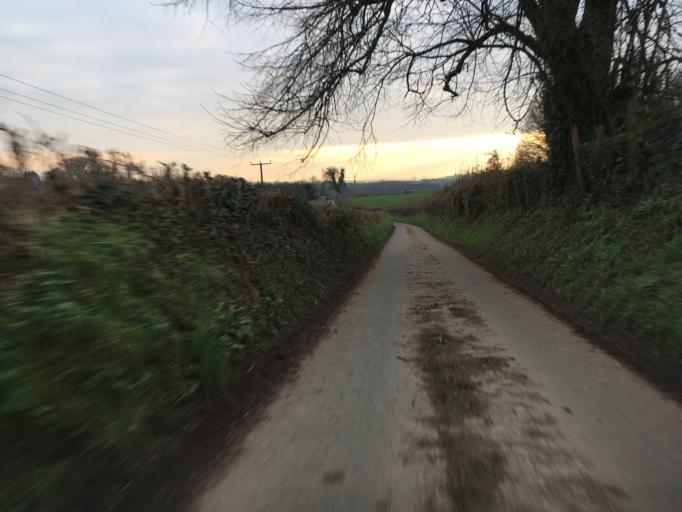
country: GB
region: Wales
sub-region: Newport
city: Marshfield
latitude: 51.5456
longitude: -3.0922
